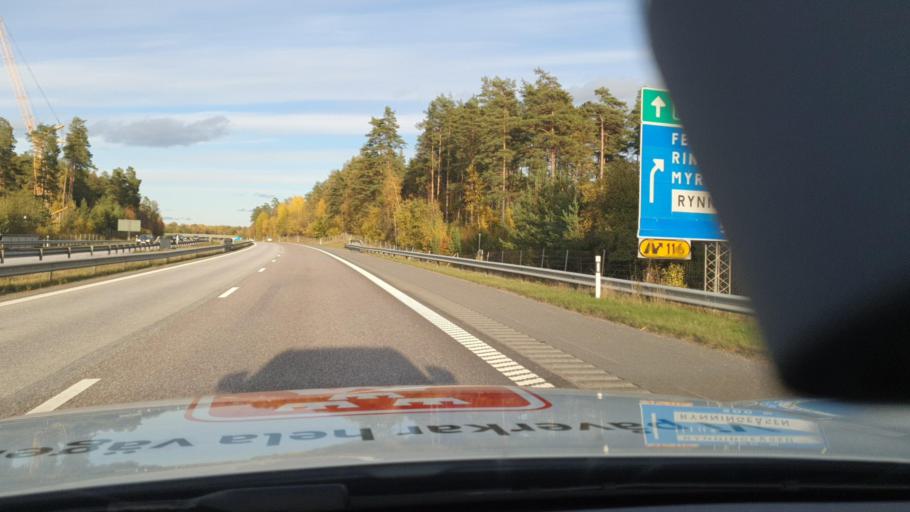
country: SE
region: OErebro
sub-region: Orebro Kommun
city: Orebro
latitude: 59.2990
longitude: 15.2457
